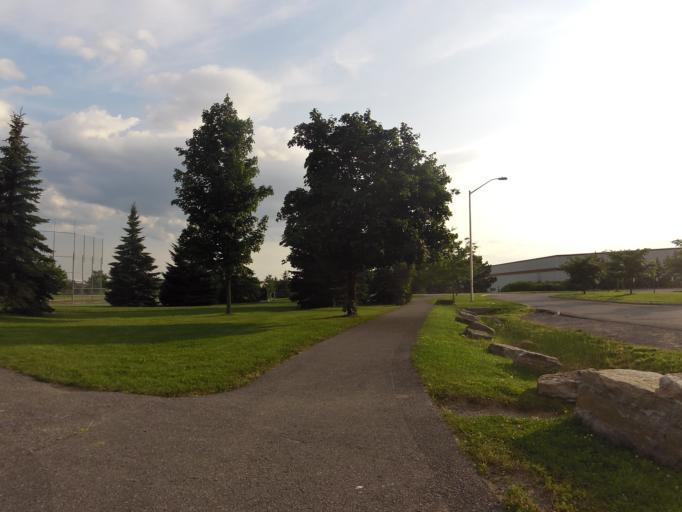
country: CA
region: Ontario
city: Bells Corners
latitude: 45.2944
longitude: -75.8996
